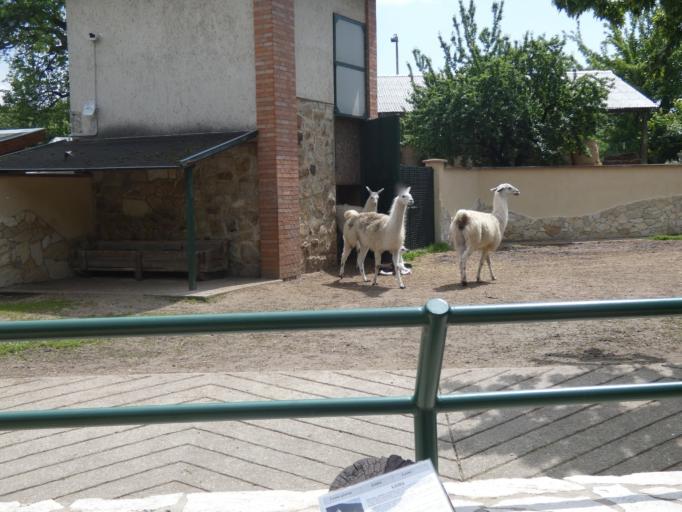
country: HU
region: Hajdu-Bihar
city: Debrecen
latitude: 47.5534
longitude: 21.6359
